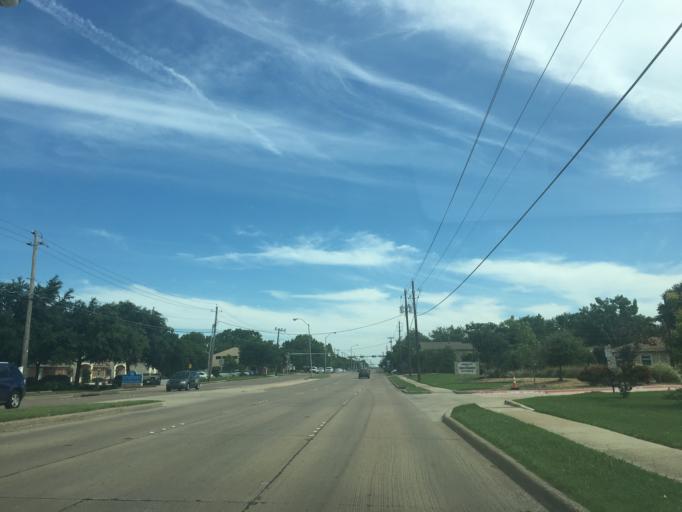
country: US
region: Texas
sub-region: Dallas County
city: Richardson
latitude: 32.9695
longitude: -96.6828
